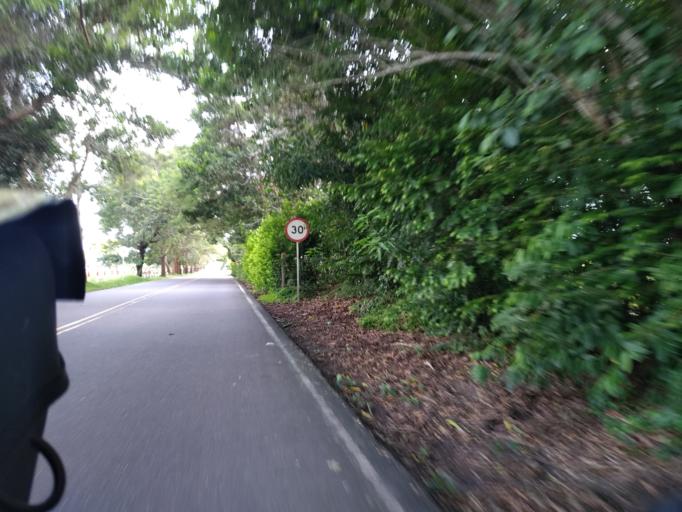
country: CO
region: Santander
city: Puerto Parra
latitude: 6.4841
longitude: -74.0379
